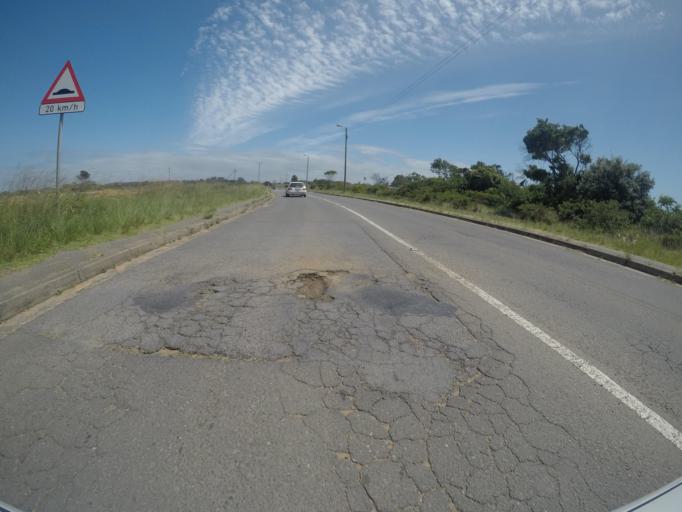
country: ZA
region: Eastern Cape
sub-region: Buffalo City Metropolitan Municipality
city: East London
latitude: -32.9464
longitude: 27.9958
